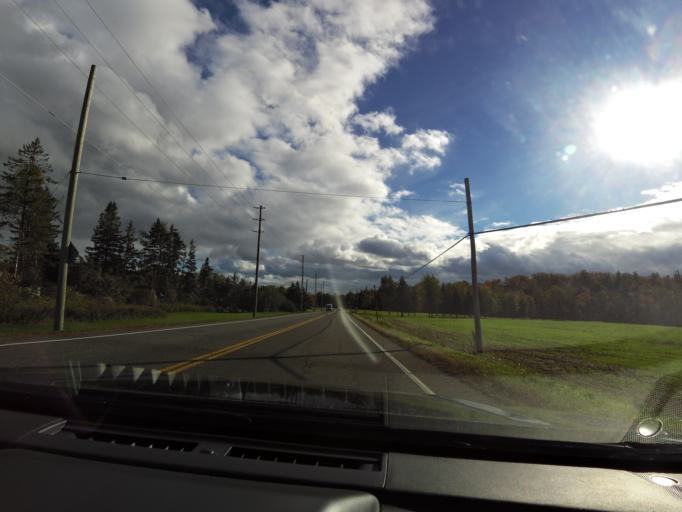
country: CA
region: Ontario
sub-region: Halton
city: Milton
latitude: 43.4547
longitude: -79.9377
